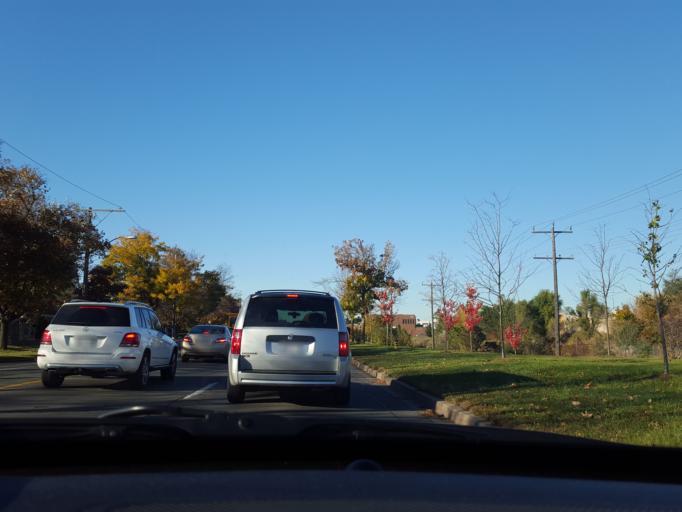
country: CA
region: Ontario
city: Scarborough
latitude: 43.7944
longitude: -79.2715
